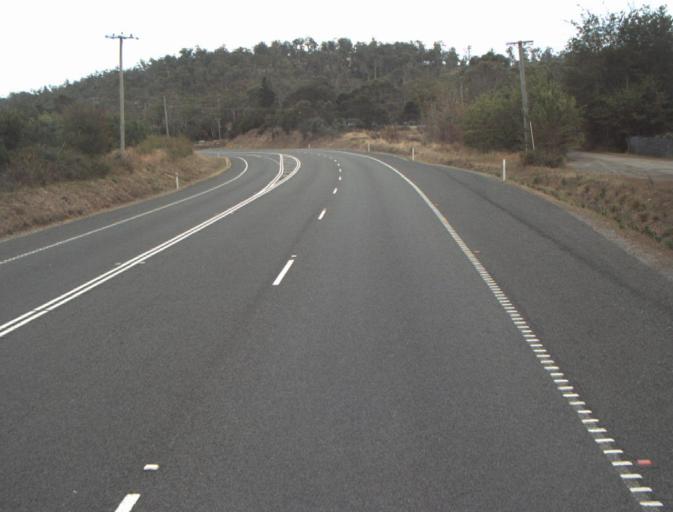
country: AU
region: Tasmania
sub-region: Launceston
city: Mayfield
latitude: -41.2457
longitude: 147.0189
